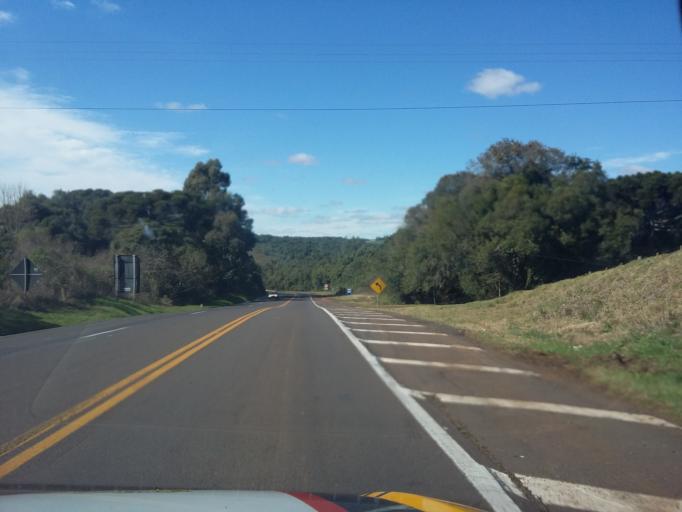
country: BR
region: Rio Grande do Sul
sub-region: Vacaria
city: Vacaria
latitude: -28.5776
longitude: -51.0212
